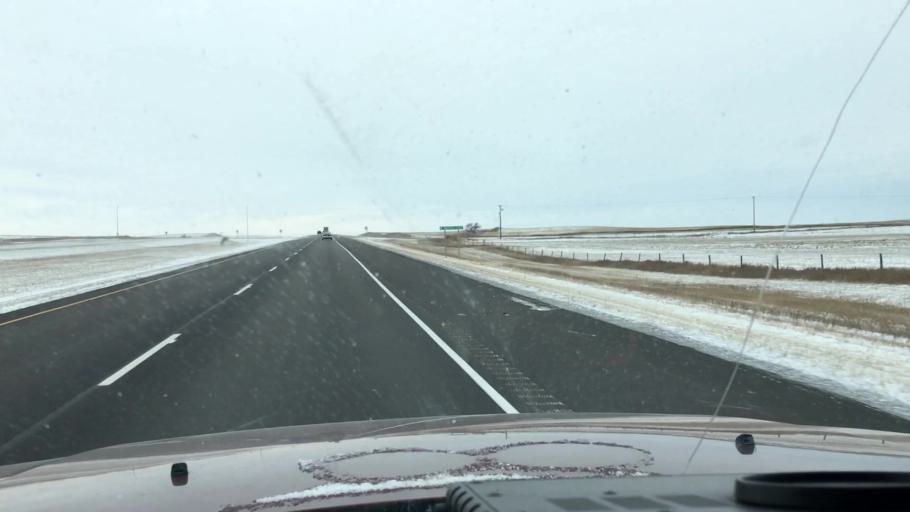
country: CA
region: Saskatchewan
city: Saskatoon
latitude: 51.7094
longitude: -106.4650
